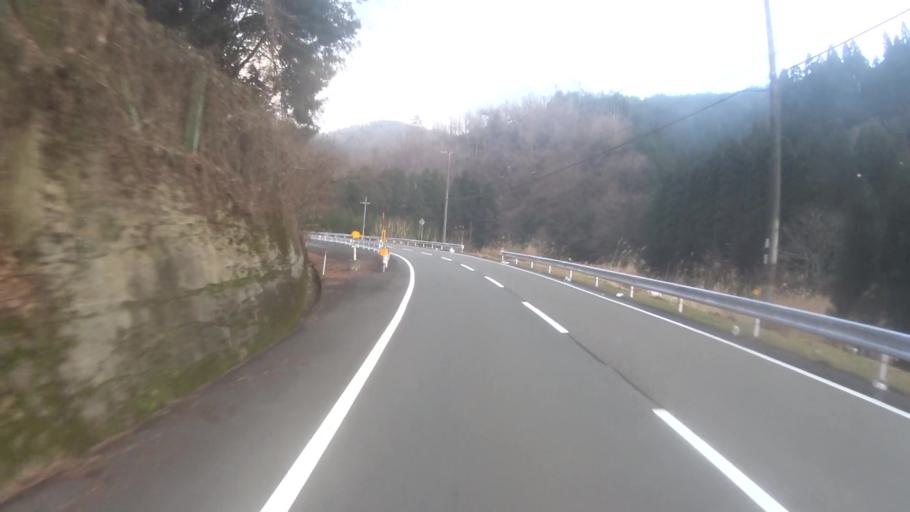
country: JP
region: Kyoto
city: Maizuru
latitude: 35.4182
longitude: 135.4660
